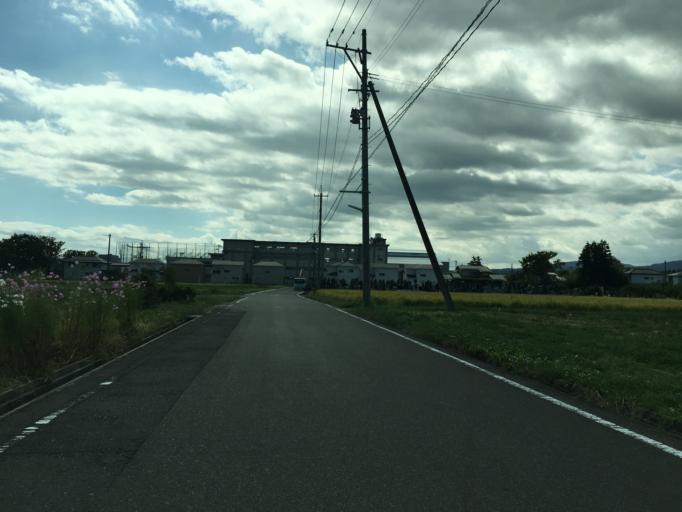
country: JP
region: Fukushima
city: Fukushima-shi
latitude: 37.7467
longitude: 140.4322
